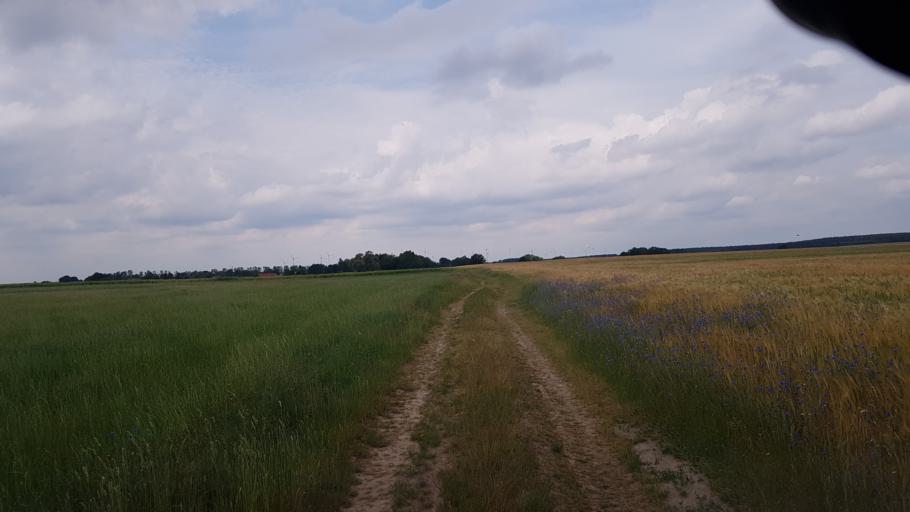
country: DE
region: Brandenburg
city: Dahme
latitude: 51.8847
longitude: 13.3946
